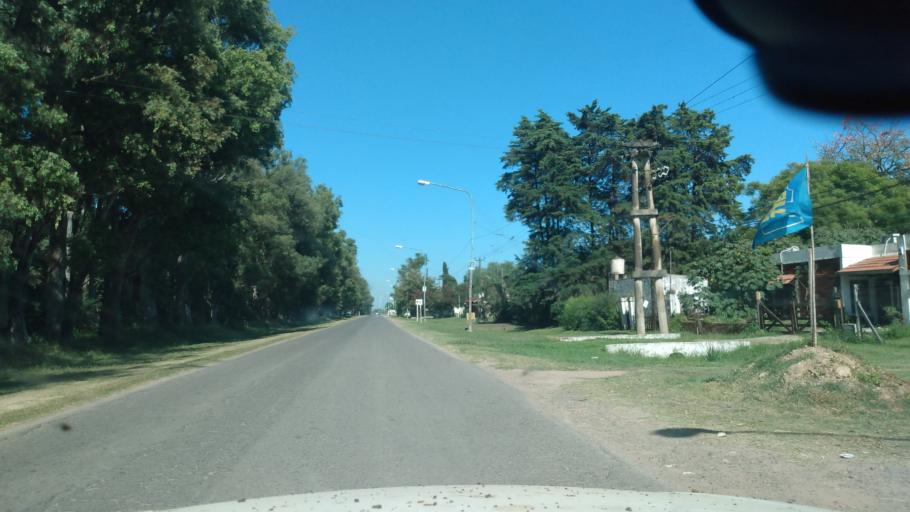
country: AR
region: Buenos Aires
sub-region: Partido de Lujan
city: Lujan
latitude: -34.5021
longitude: -59.0713
